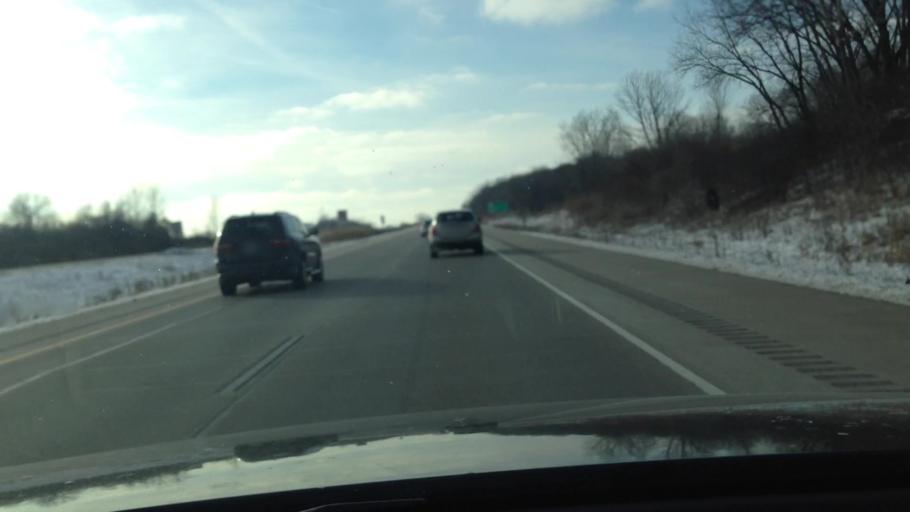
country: US
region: Wisconsin
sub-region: Waukesha County
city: Muskego
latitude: 42.9308
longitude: -88.1703
